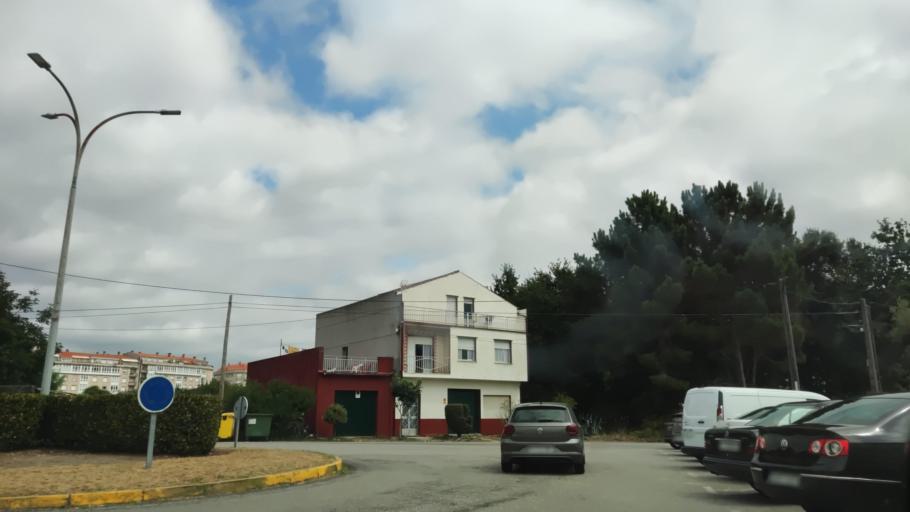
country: ES
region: Galicia
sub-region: Provincia da Coruna
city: Boiro
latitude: 42.6426
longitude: -8.8908
